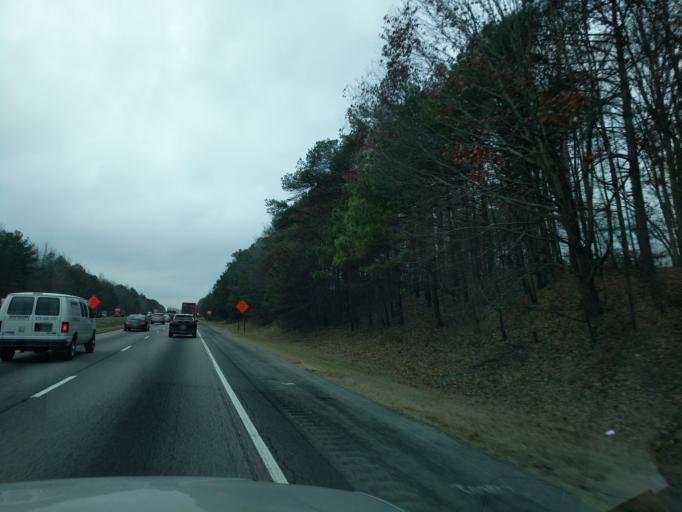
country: US
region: Georgia
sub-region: Barrow County
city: Auburn
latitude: 34.0822
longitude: -83.8751
